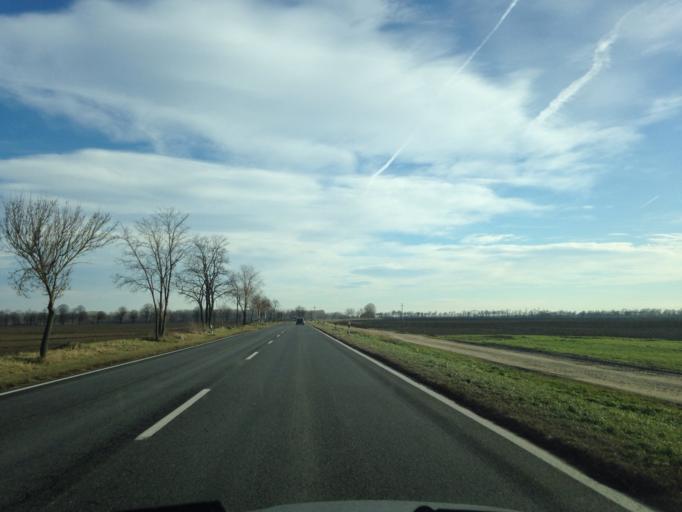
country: HU
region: Gyor-Moson-Sopron
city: Kimle
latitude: 47.8271
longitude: 17.3204
